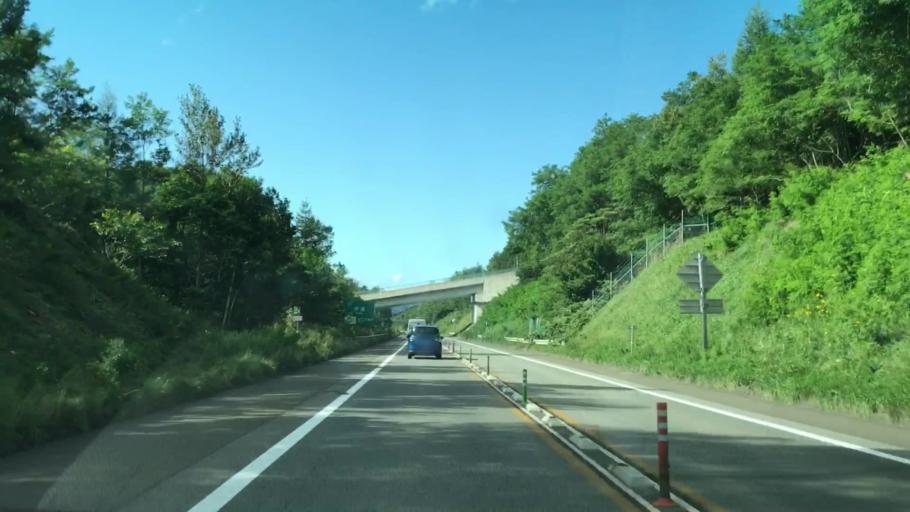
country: JP
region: Hokkaido
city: Date
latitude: 42.4717
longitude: 140.9054
